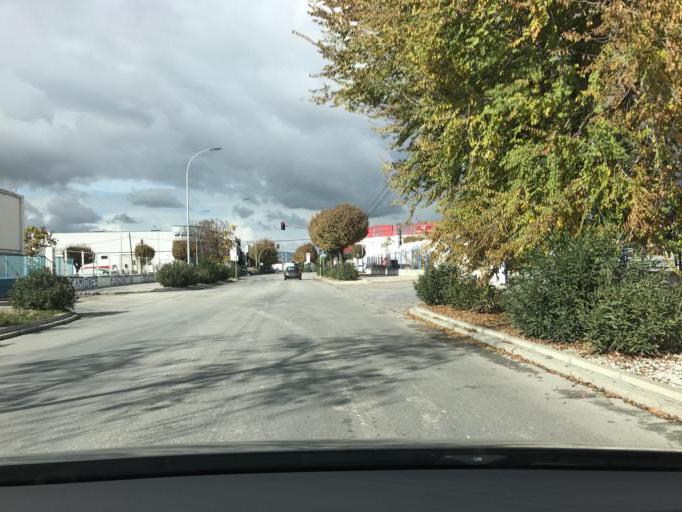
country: ES
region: Andalusia
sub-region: Provincia de Granada
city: Albolote
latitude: 37.2238
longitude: -3.6427
